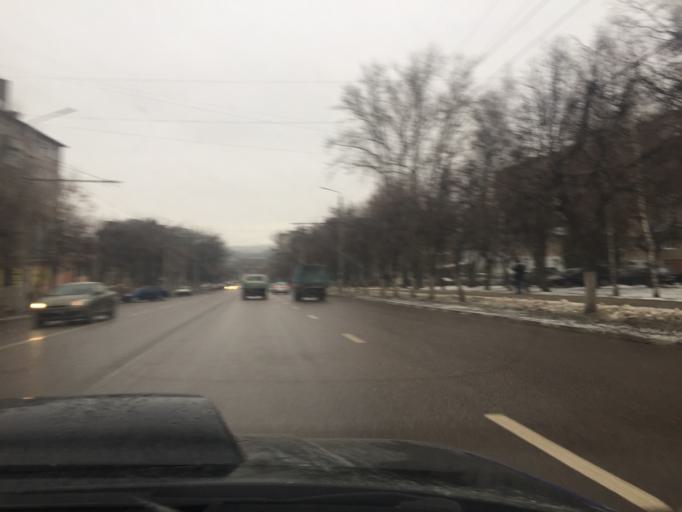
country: RU
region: Tula
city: Tula
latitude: 54.1926
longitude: 37.5842
